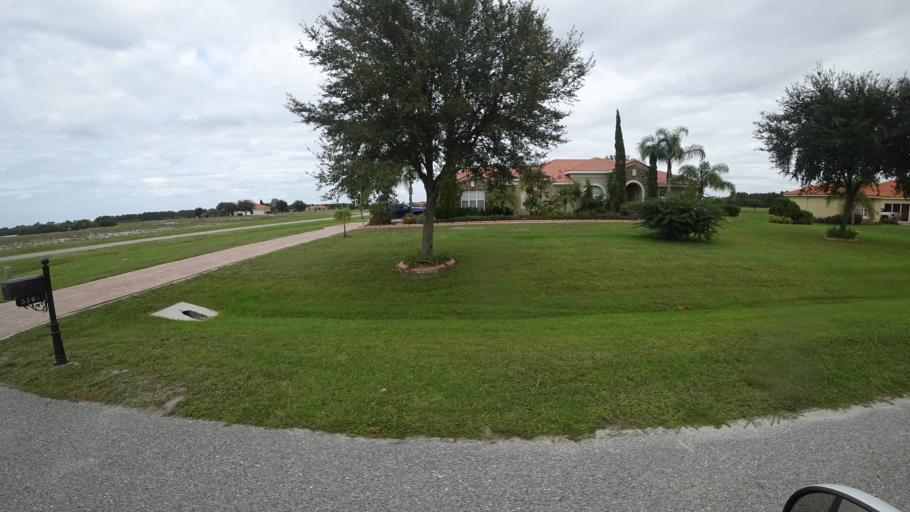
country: US
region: Florida
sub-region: Hillsborough County
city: Wimauma
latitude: 27.6535
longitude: -82.3280
